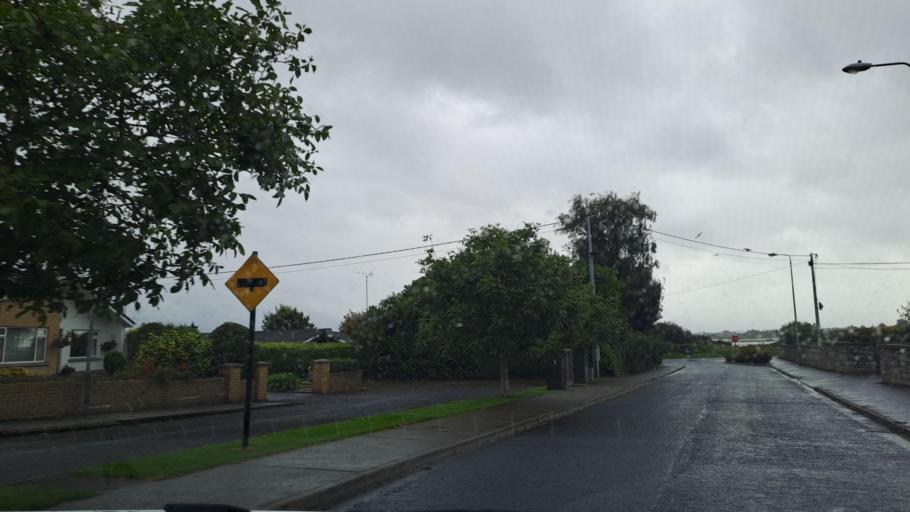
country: IE
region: Leinster
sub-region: Lu
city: Blackrock
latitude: 53.9582
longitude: -6.3753
